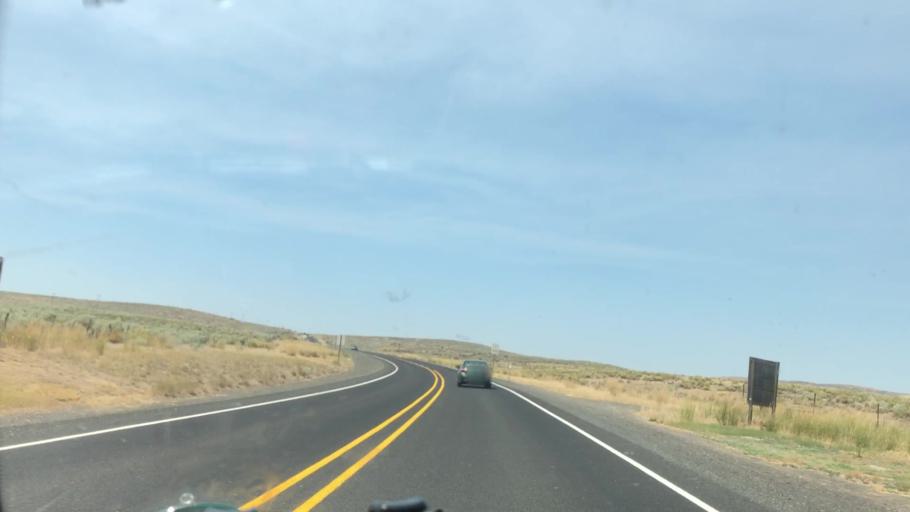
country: US
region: Idaho
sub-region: Owyhee County
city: Murphy
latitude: 42.9826
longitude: -117.0531
